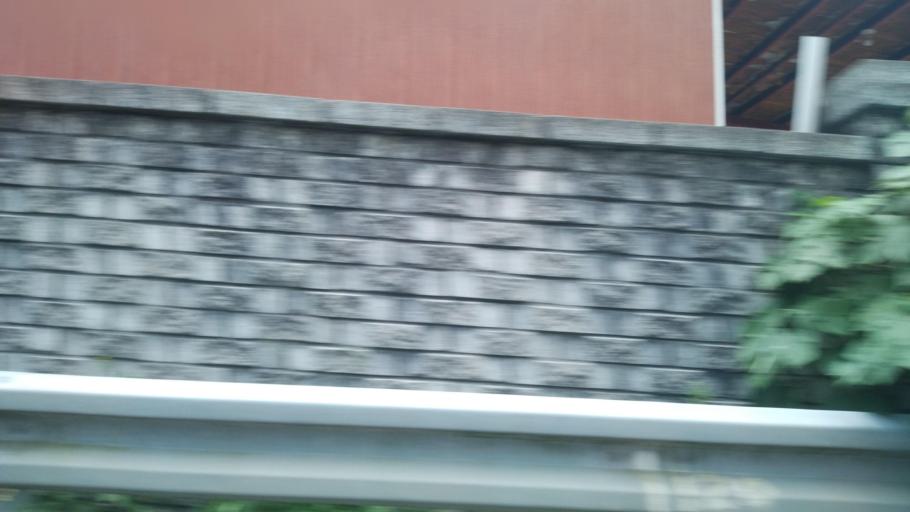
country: TW
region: Taipei
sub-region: Taipei
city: Banqiao
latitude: 24.9275
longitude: 121.4468
